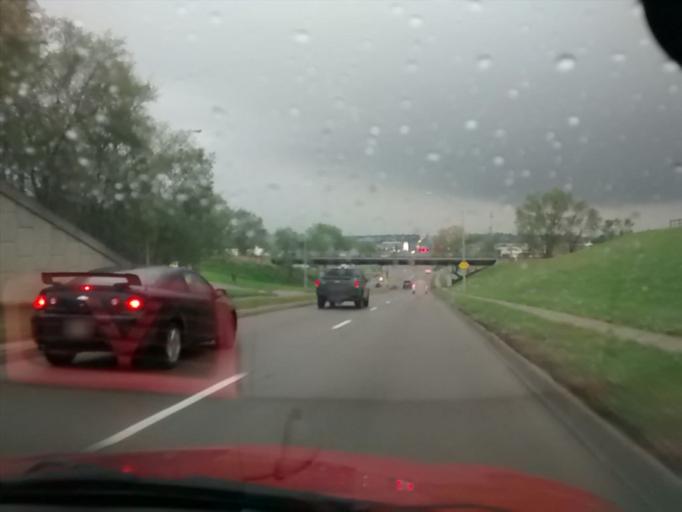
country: US
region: Nebraska
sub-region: Sarpy County
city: La Vista
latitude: 41.1978
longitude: -96.0237
